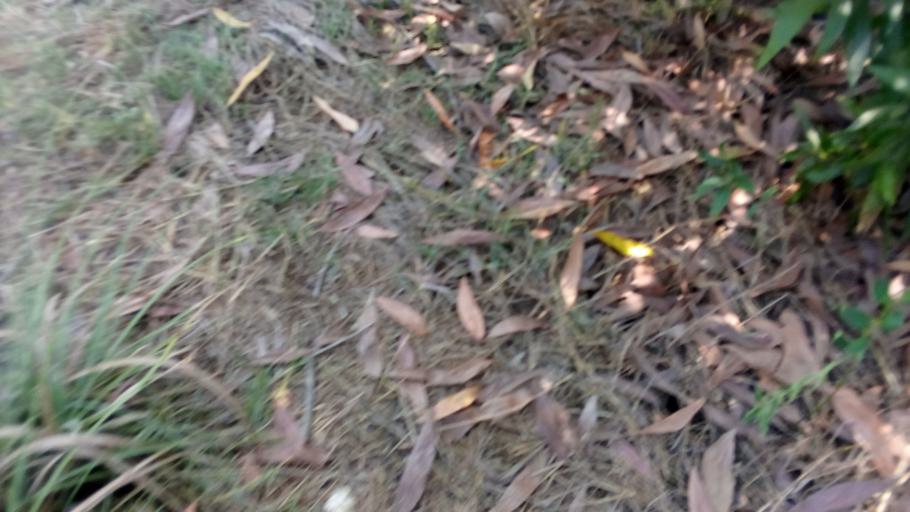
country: GN
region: Kindia
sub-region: Prefecture de Dubreka
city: Dubreka
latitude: 9.7834
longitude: -13.5211
